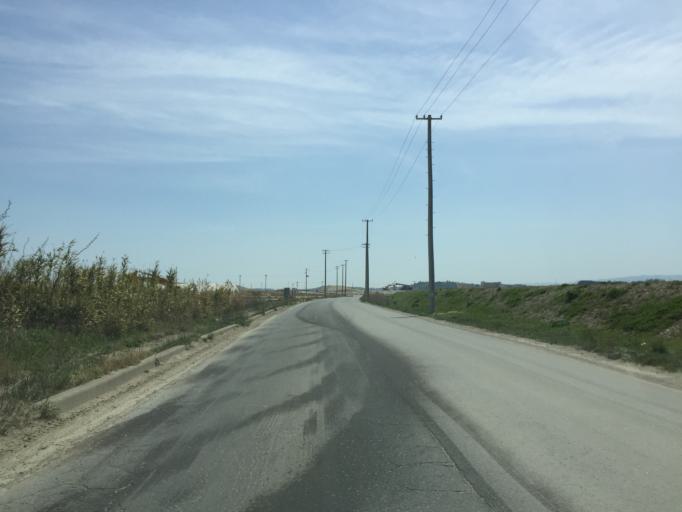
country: JP
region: Miyagi
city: Watari
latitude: 37.9364
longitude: 140.9119
